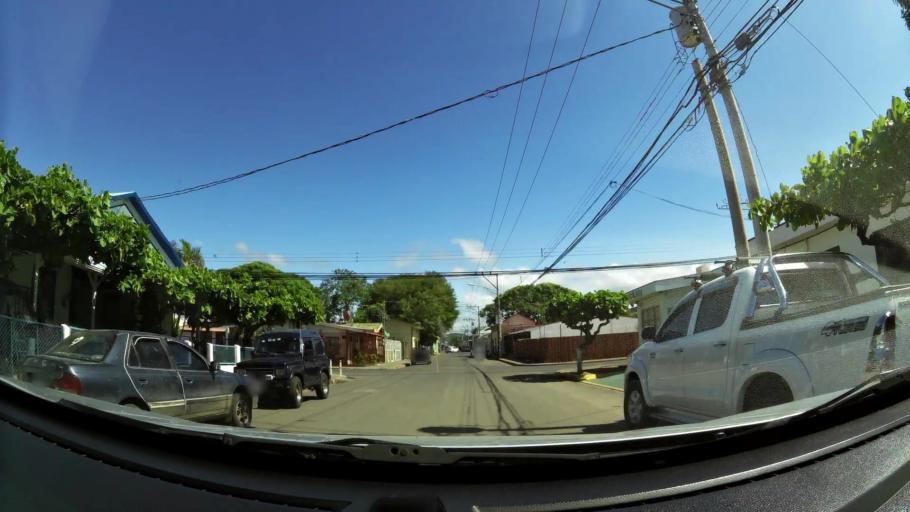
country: CR
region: Guanacaste
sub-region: Canton de Canas
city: Canas
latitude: 10.4269
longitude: -85.0932
